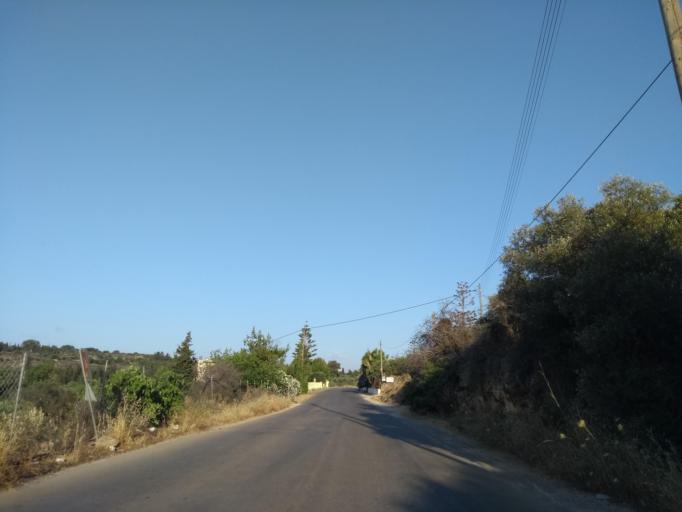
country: GR
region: Crete
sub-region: Nomos Chanias
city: Kalivai
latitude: 35.4183
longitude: 24.1894
